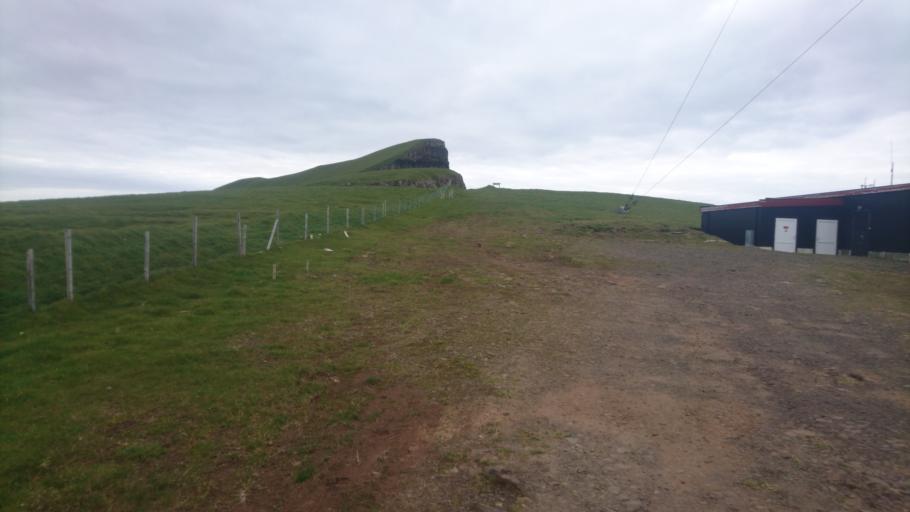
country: FO
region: Suduroy
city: Vagur
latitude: 61.4236
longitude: -6.7539
